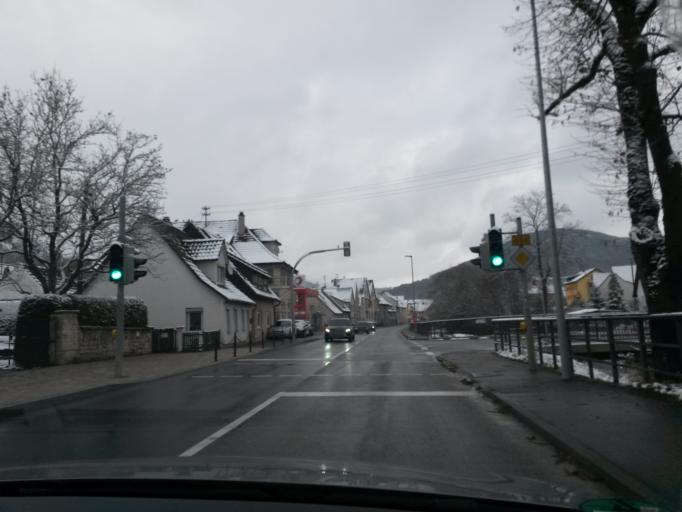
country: DE
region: Baden-Wuerttemberg
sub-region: Regierungsbezirk Stuttgart
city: Deggingen
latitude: 48.5965
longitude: 9.7150
